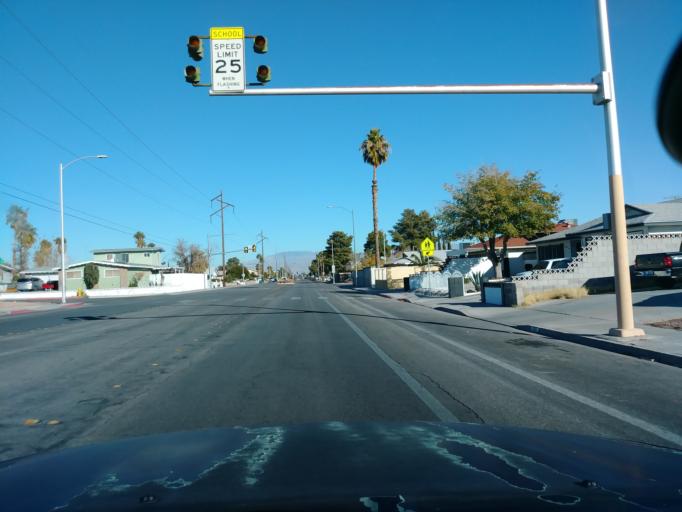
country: US
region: Nevada
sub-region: Clark County
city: Spring Valley
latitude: 36.1694
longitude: -115.2508
